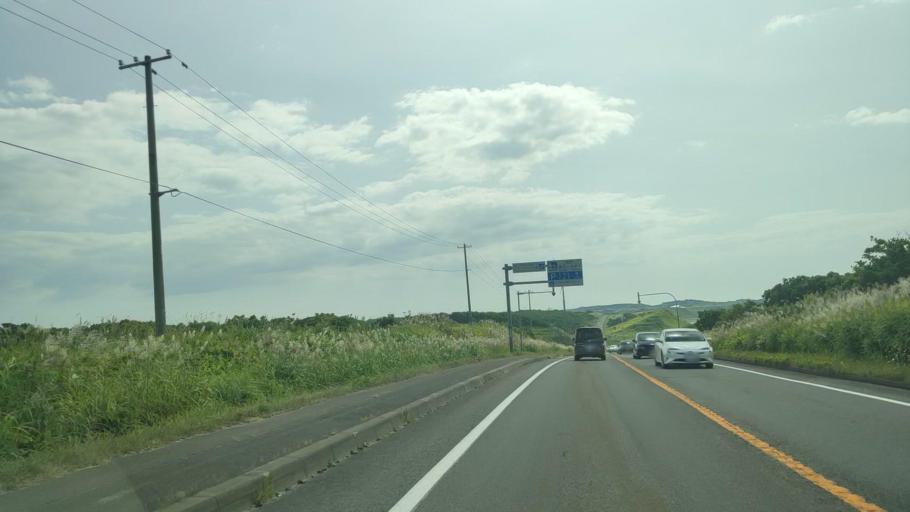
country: JP
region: Hokkaido
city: Rumoi
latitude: 44.3267
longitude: 141.6760
